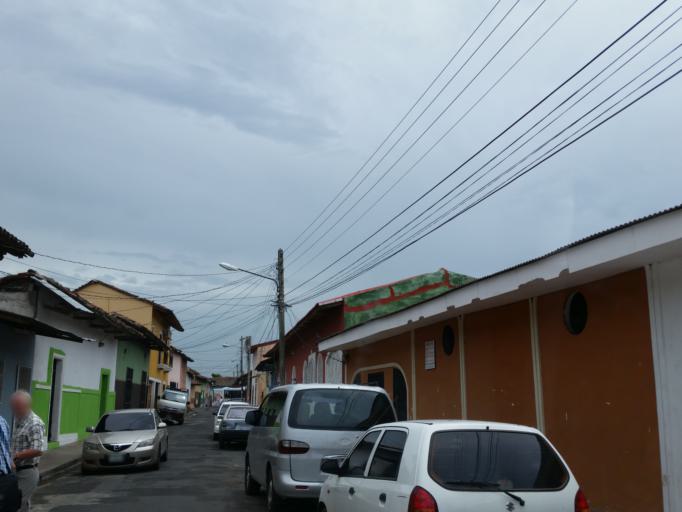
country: NI
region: Granada
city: Granada
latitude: 11.9315
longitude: -85.9579
